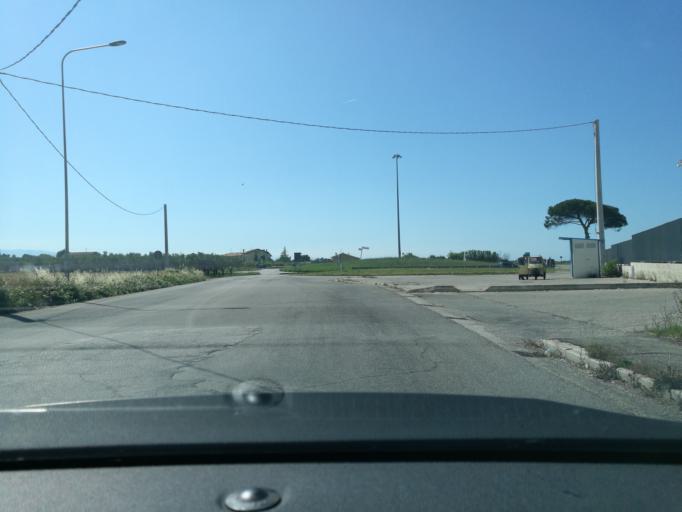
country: IT
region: Abruzzo
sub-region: Provincia di Chieti
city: Vasto
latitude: 42.1652
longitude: 14.6838
